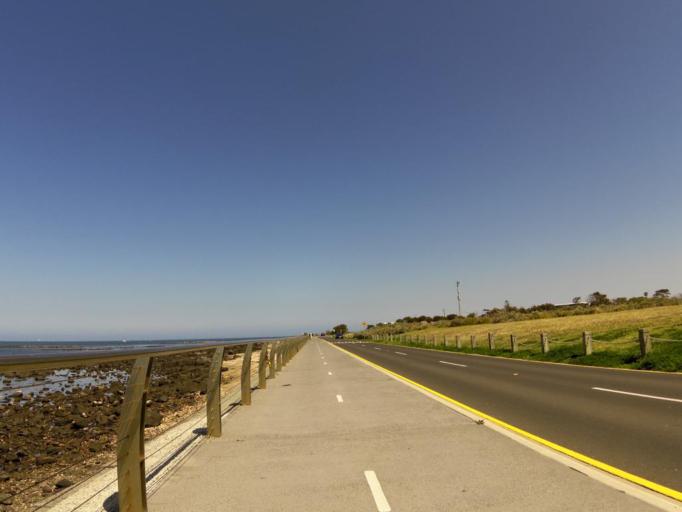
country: AU
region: Victoria
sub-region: Hobsons Bay
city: Williamstown
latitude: -37.8684
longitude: 144.9113
